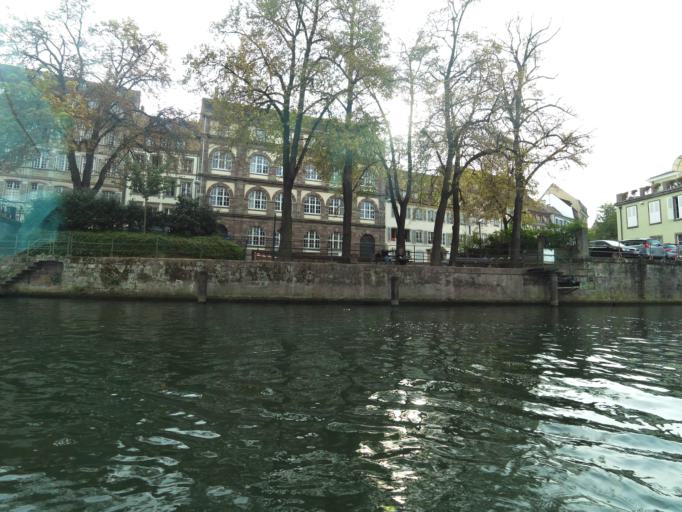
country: FR
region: Alsace
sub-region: Departement du Bas-Rhin
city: Strasbourg
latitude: 48.5791
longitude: 7.7446
